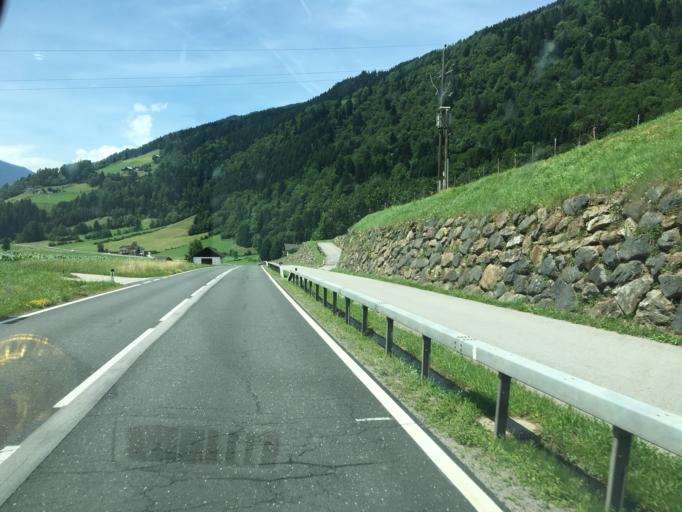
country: AT
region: Carinthia
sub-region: Politischer Bezirk Spittal an der Drau
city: Rangersdorf
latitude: 46.8711
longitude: 12.9860
